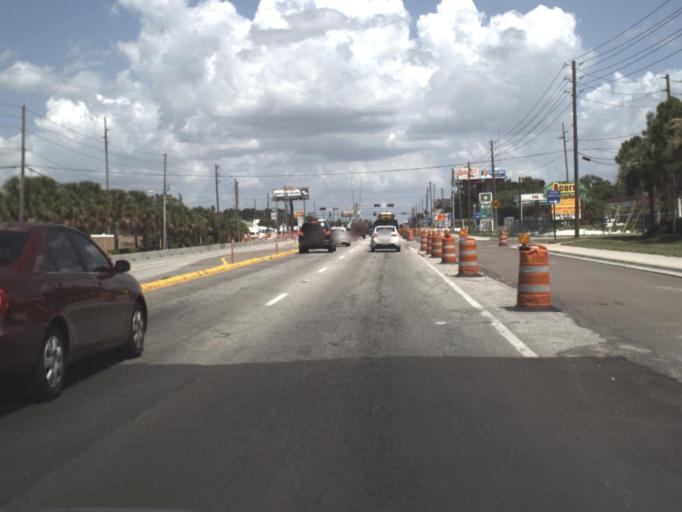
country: US
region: Florida
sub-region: Pinellas County
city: Largo
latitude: 27.8945
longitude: -82.7741
